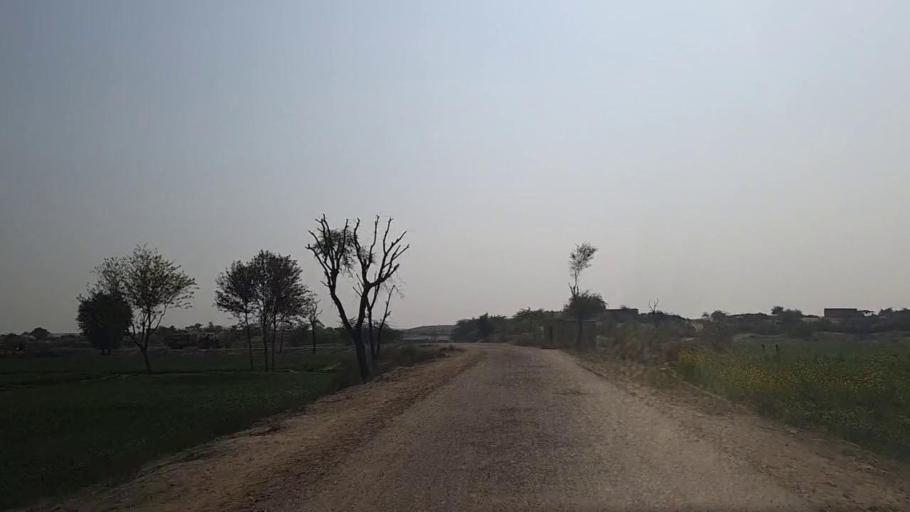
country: PK
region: Sindh
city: Jam Sahib
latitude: 26.4371
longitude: 68.5262
